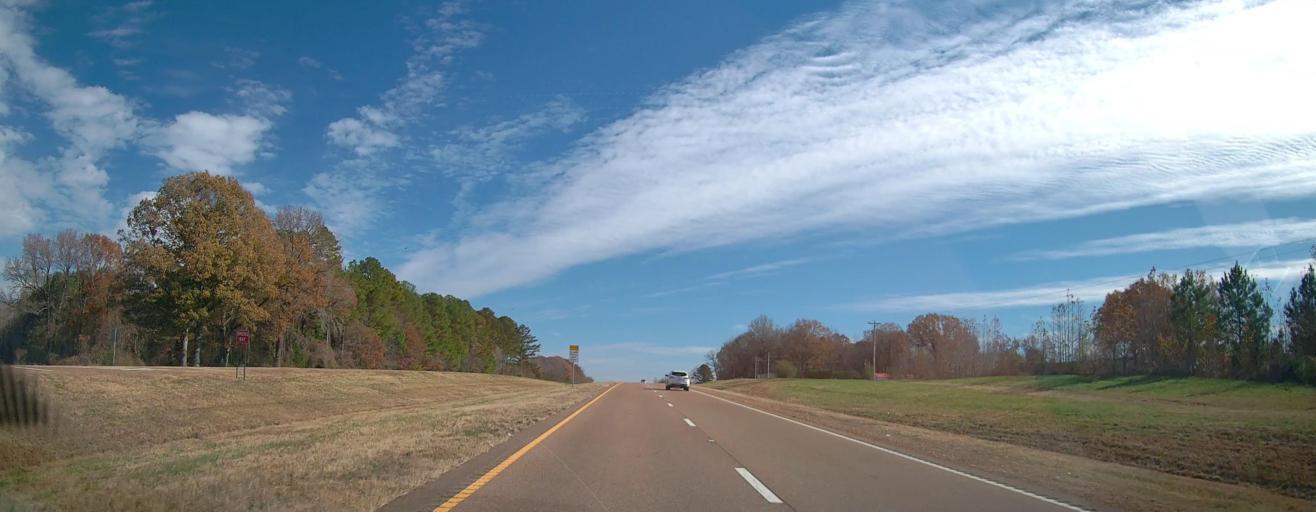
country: US
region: Mississippi
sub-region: Benton County
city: Ashland
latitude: 34.9462
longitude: -89.2885
